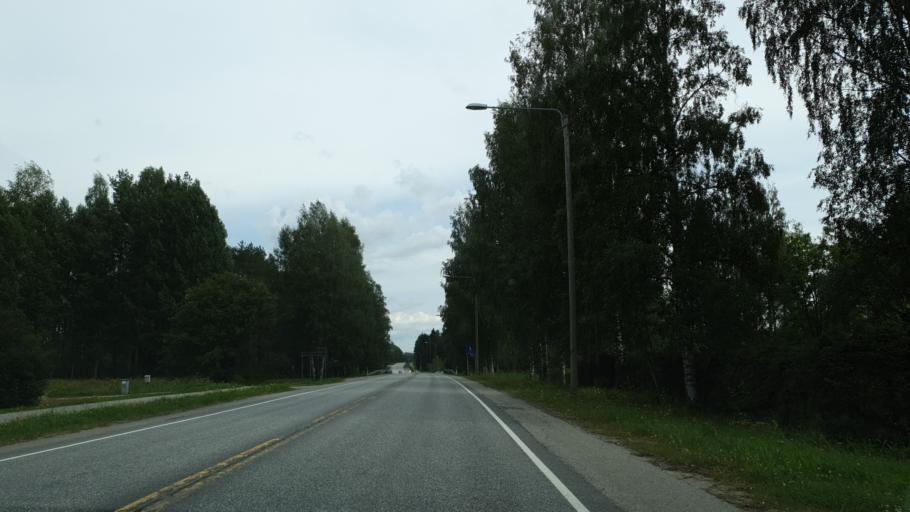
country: FI
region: North Karelia
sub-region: Pielisen Karjala
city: Valtimo
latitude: 63.6852
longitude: 28.8013
